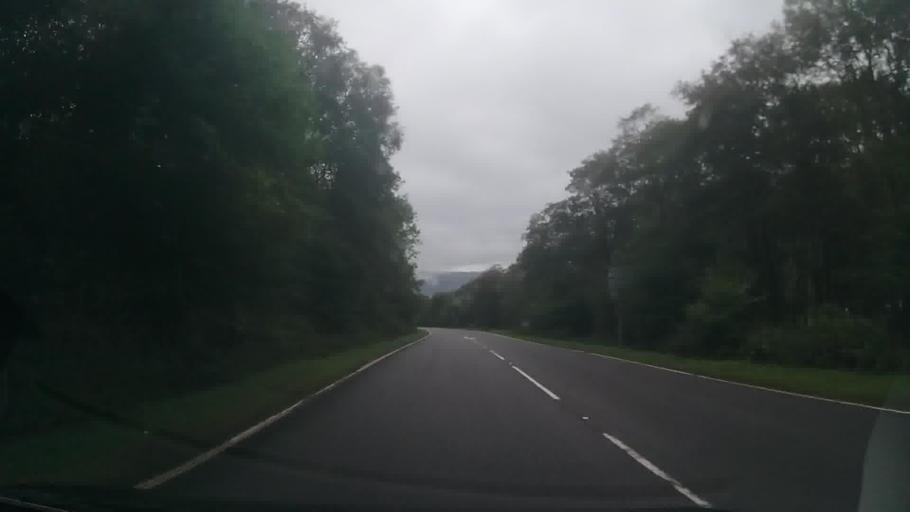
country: GB
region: Scotland
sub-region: Highland
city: Fort William
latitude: 56.6713
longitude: -5.0793
